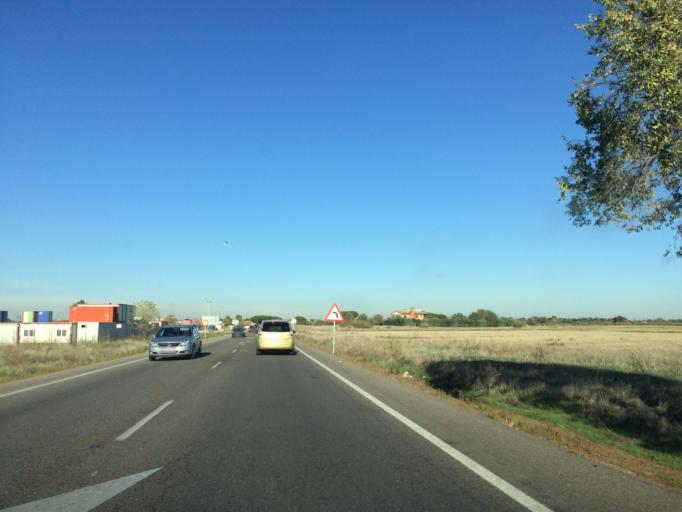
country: ES
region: Madrid
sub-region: Provincia de Madrid
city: Serranillos del Valle
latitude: 40.1875
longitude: -3.8806
